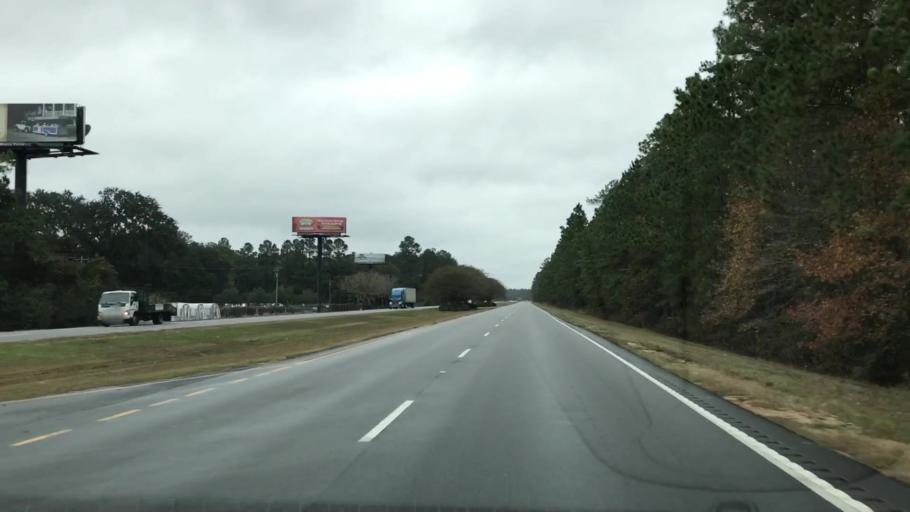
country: US
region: South Carolina
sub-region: Georgetown County
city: Georgetown
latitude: 33.2347
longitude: -79.3759
